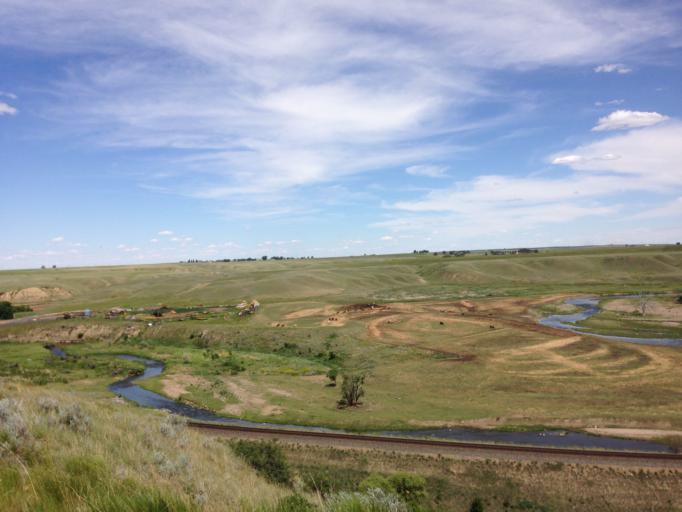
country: CA
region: Alberta
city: Medicine Hat
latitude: 50.0128
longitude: -110.6226
